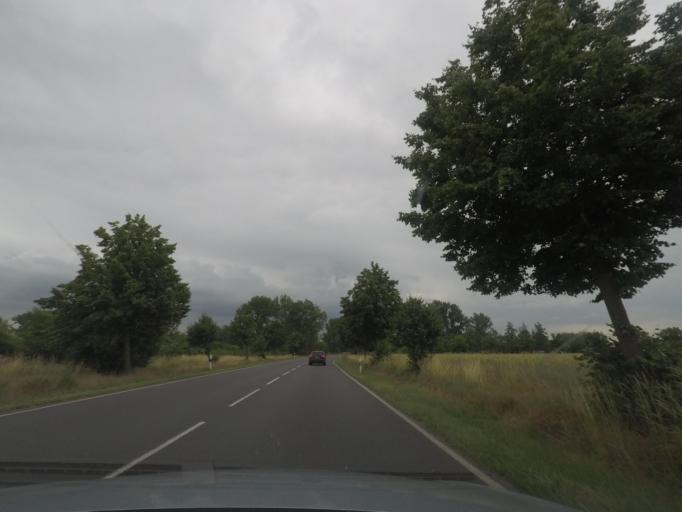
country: DE
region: Saxony-Anhalt
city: Haldensleben I
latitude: 52.2891
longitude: 11.4346
